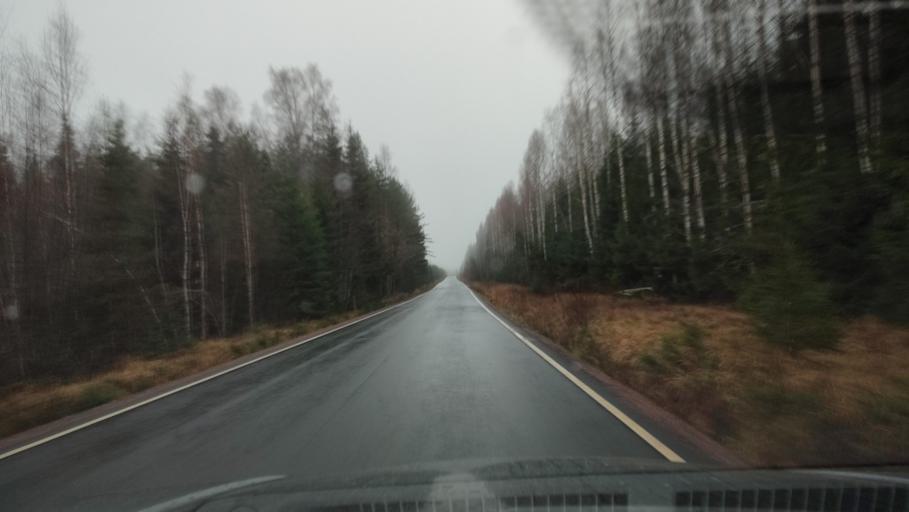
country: FI
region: Southern Ostrobothnia
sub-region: Suupohja
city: Karijoki
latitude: 62.1551
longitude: 21.7144
